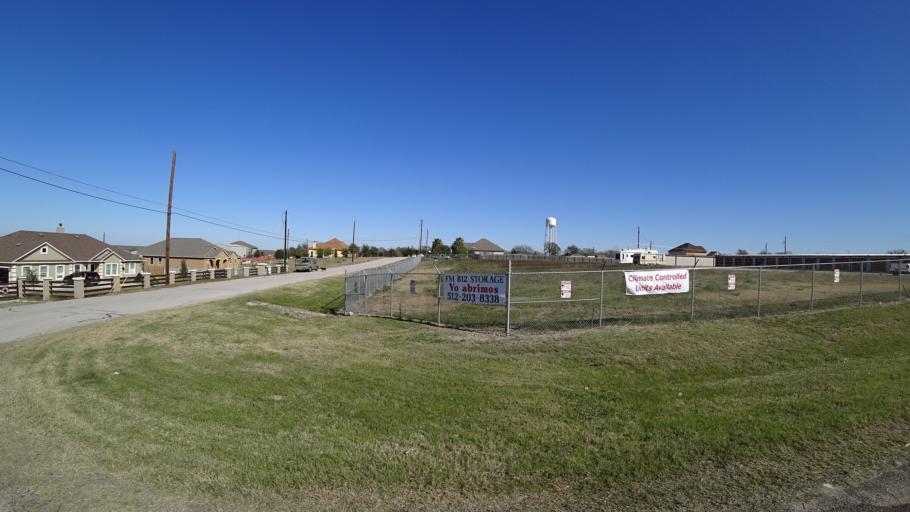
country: US
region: Texas
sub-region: Travis County
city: Garfield
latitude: 30.0977
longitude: -97.6031
